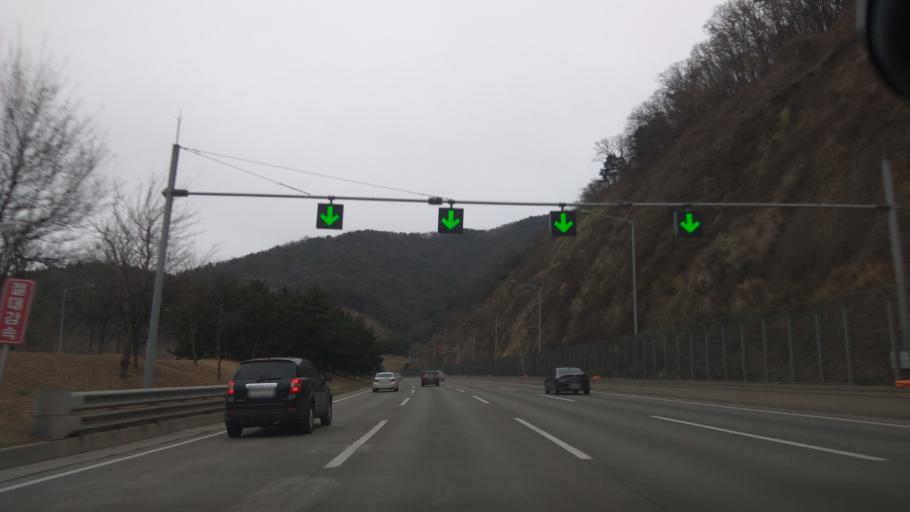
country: KR
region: Gyeonggi-do
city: Jangheung
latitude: 37.6845
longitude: 126.9318
